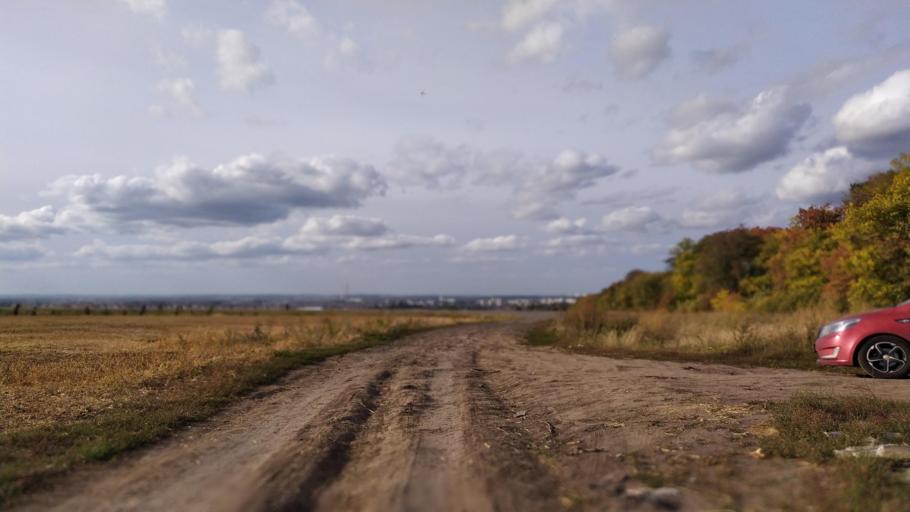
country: RU
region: Kursk
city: Kursk
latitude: 51.6129
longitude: 36.1651
